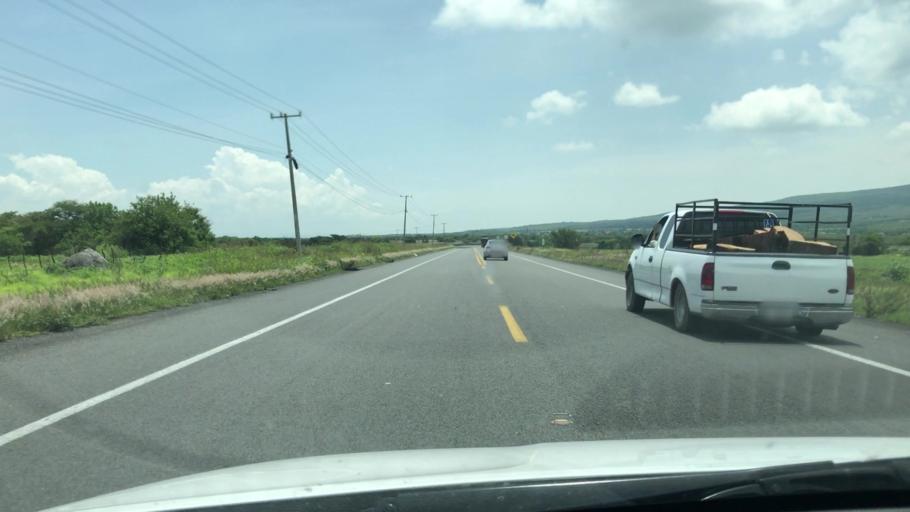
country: MX
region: Michoacan
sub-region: Yurecuaro
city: Yurecuaro
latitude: 20.3418
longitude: -102.1665
